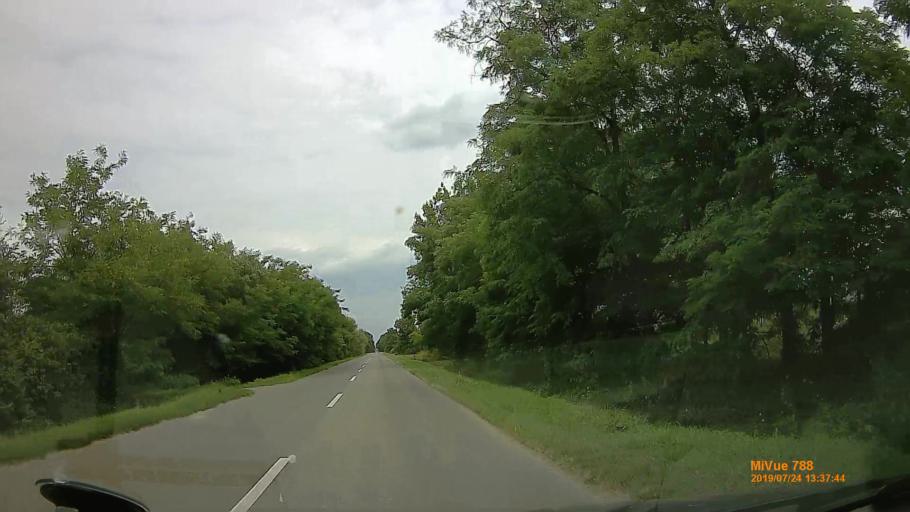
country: HU
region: Szabolcs-Szatmar-Bereg
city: Aranyosapati
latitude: 48.2291
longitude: 22.3070
